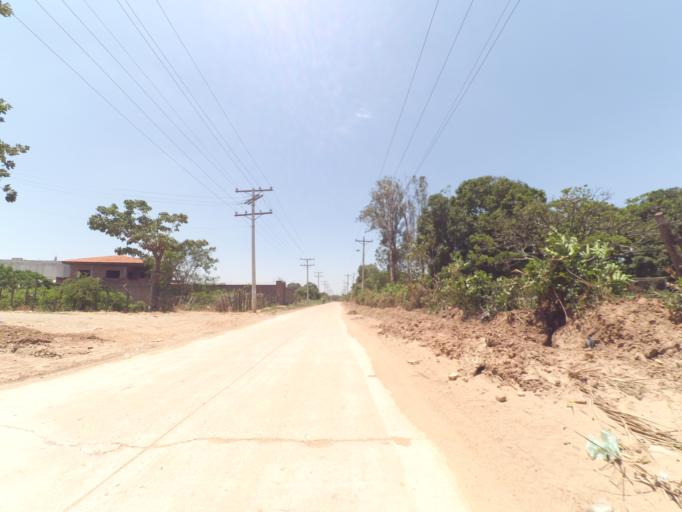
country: BO
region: Santa Cruz
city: Santa Cruz de la Sierra
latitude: -17.8609
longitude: -63.2319
